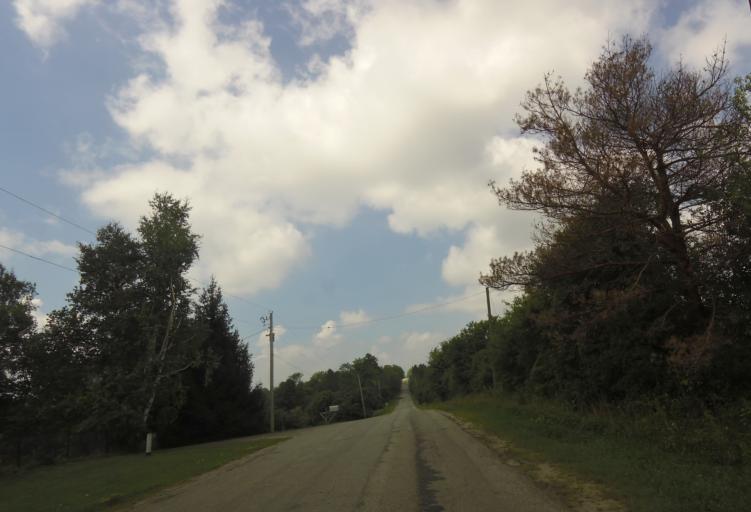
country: CA
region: Ontario
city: Oshawa
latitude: 43.9957
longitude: -78.8741
